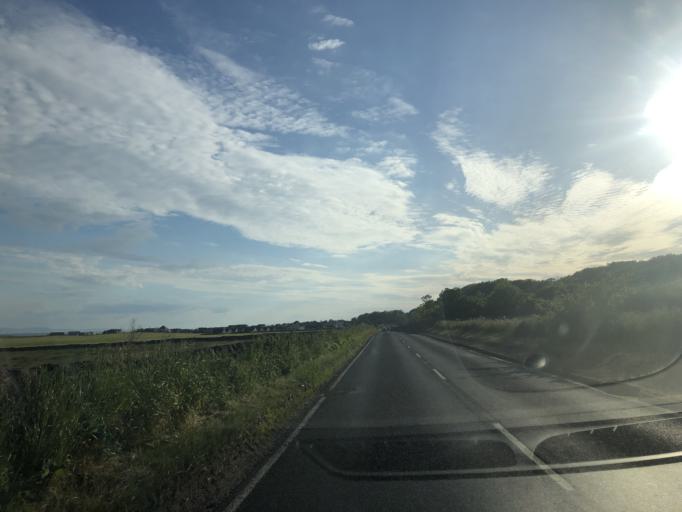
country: GB
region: Scotland
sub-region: Fife
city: Saint Monance
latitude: 56.1935
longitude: -2.8048
